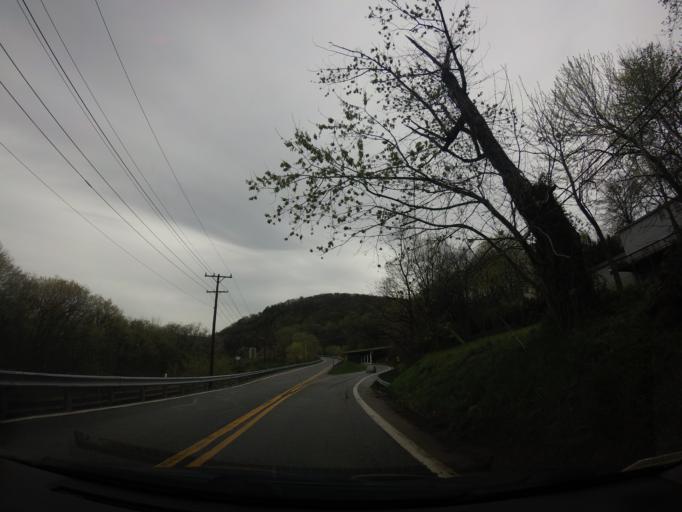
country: US
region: Maryland
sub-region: Frederick County
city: Brunswick
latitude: 39.3291
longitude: -77.6690
